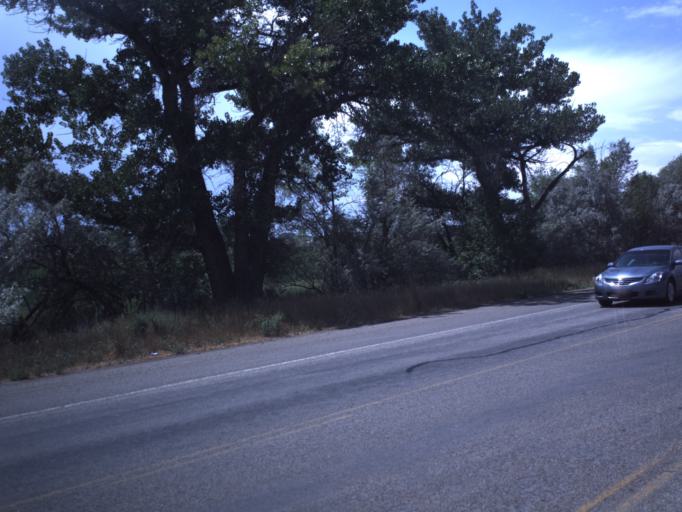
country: US
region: Utah
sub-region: Duchesne County
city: Roosevelt
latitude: 40.3023
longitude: -109.9682
